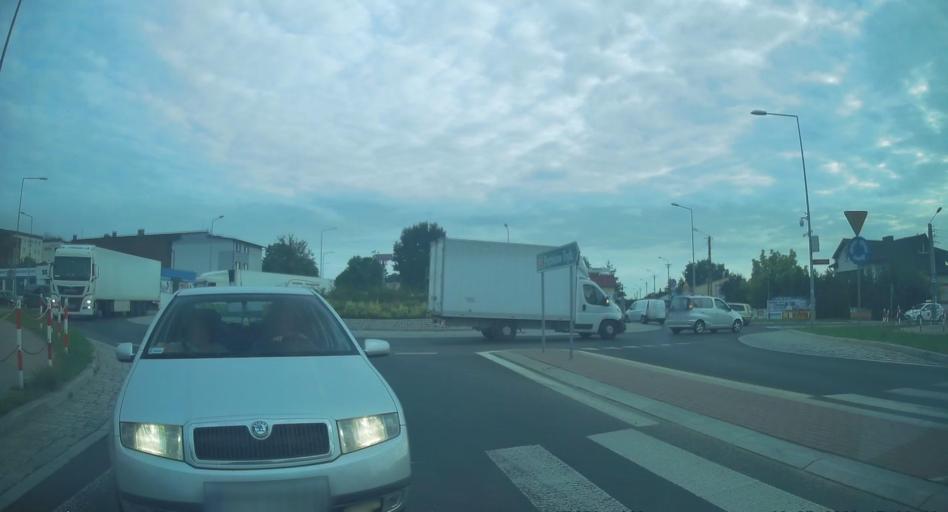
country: PL
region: Lodz Voivodeship
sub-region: Powiat radomszczanski
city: Radomsko
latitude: 51.0625
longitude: 19.4422
